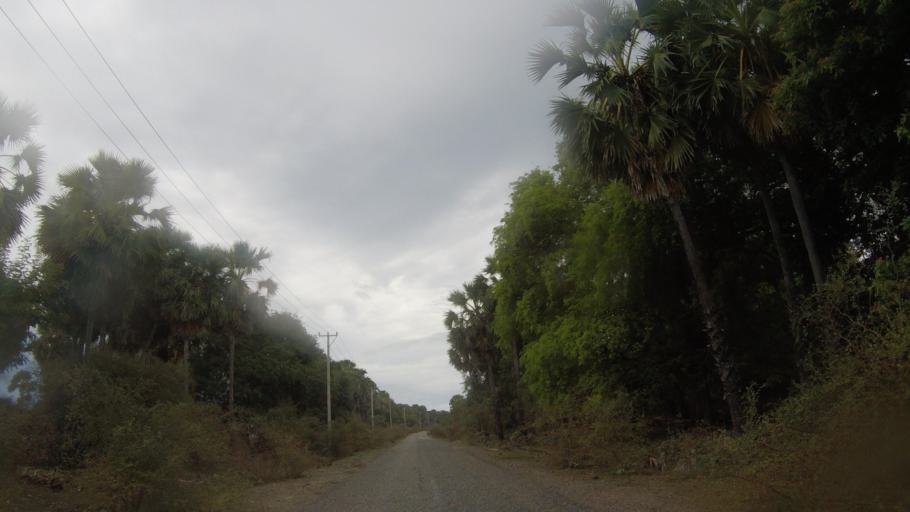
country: TL
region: Lautem
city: Lospalos
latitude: -8.3447
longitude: 126.9269
